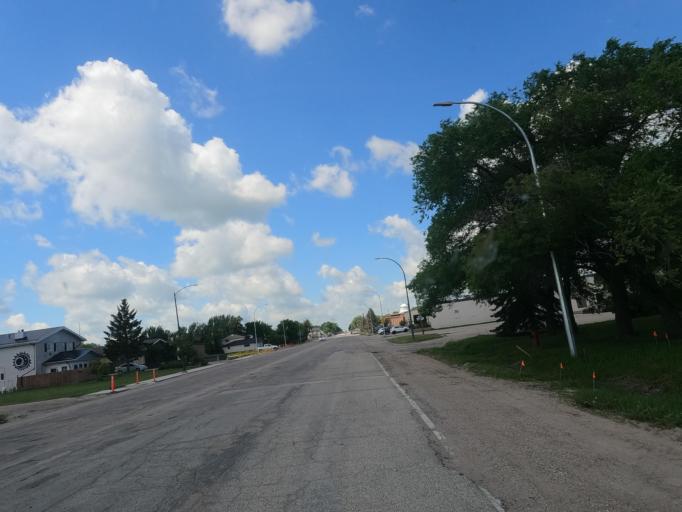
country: CA
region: Manitoba
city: Beausejour
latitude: 50.0618
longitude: -96.5038
